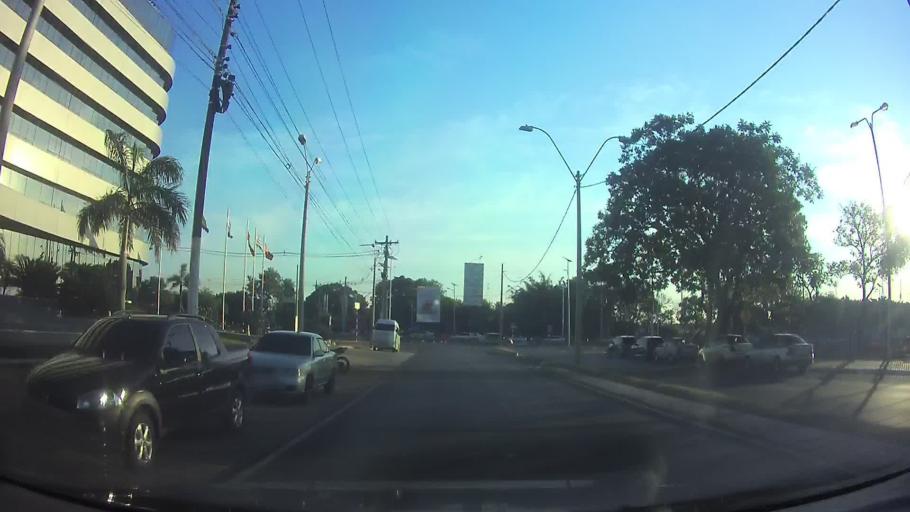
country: PY
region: Central
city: Fernando de la Mora
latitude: -25.2619
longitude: -57.5160
